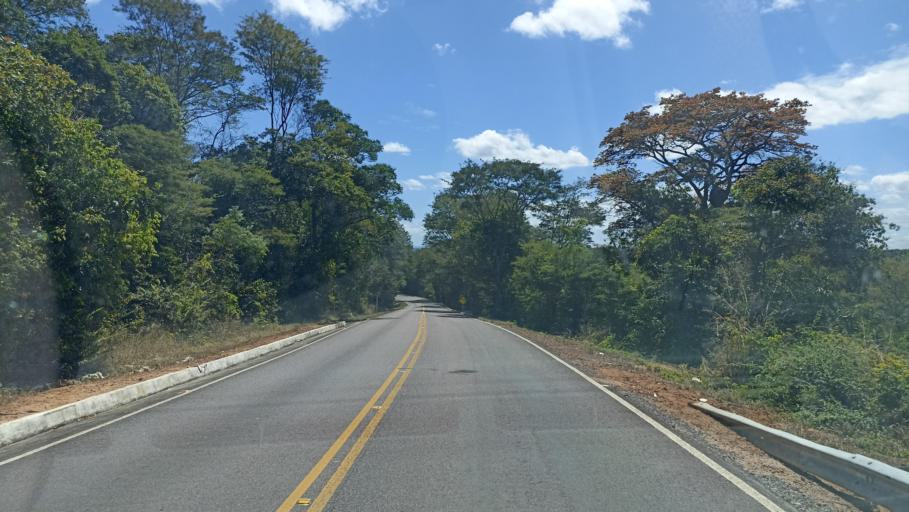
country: BR
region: Bahia
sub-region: Andarai
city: Vera Cruz
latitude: -12.7645
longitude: -41.3252
